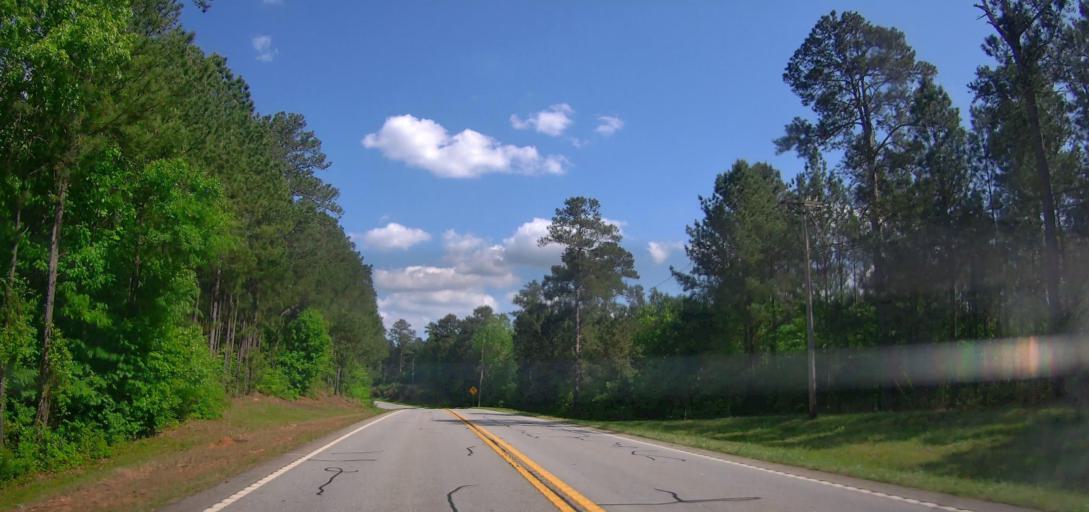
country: US
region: Georgia
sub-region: Greene County
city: Greensboro
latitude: 33.5773
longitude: -83.2640
